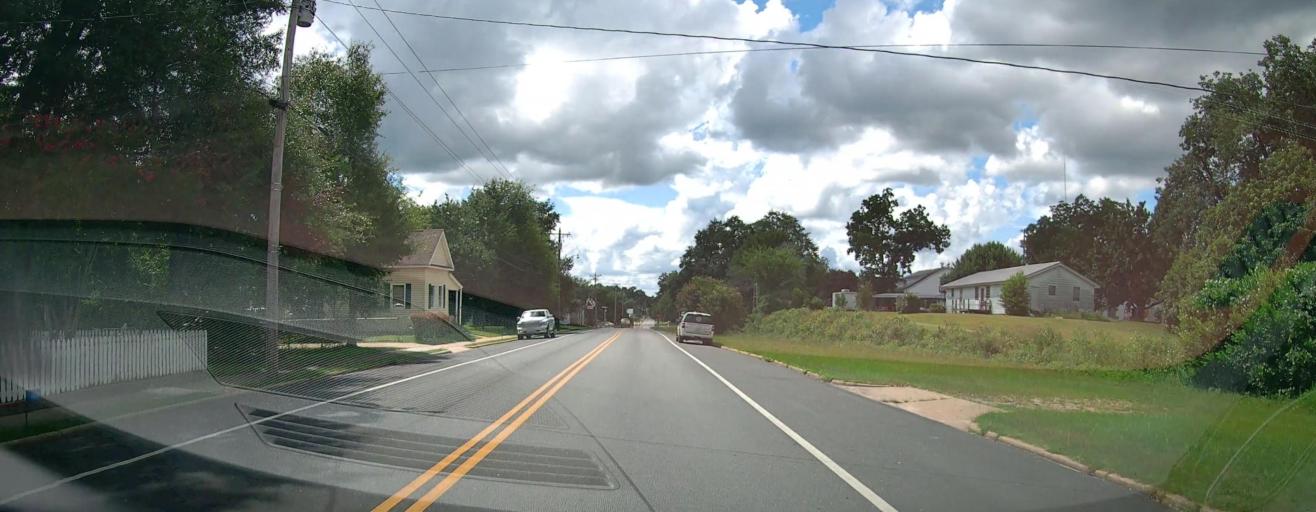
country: US
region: Georgia
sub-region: Chattahoochee County
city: Cusseta
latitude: 32.3056
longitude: -84.7748
